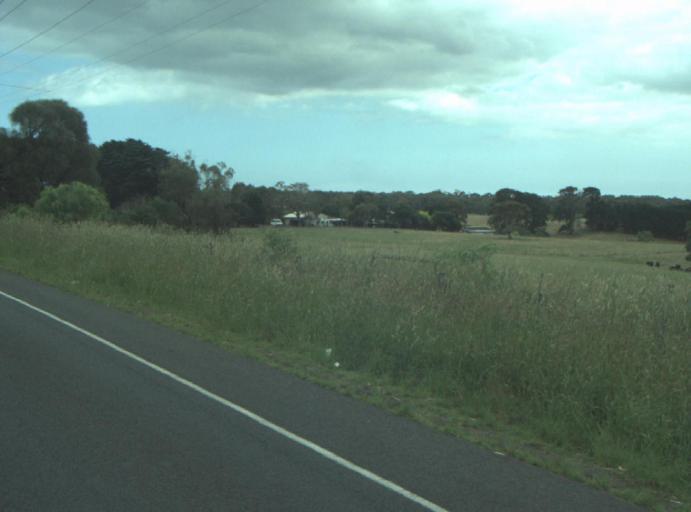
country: AU
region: Victoria
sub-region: Greater Geelong
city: Leopold
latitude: -38.2174
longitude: 144.5060
